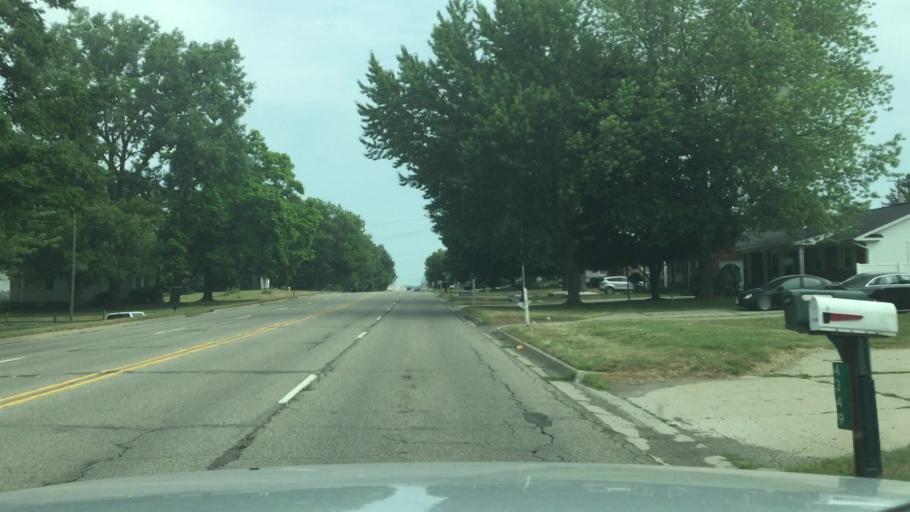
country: US
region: Michigan
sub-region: Genesee County
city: Flint
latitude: 42.9643
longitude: -83.7124
